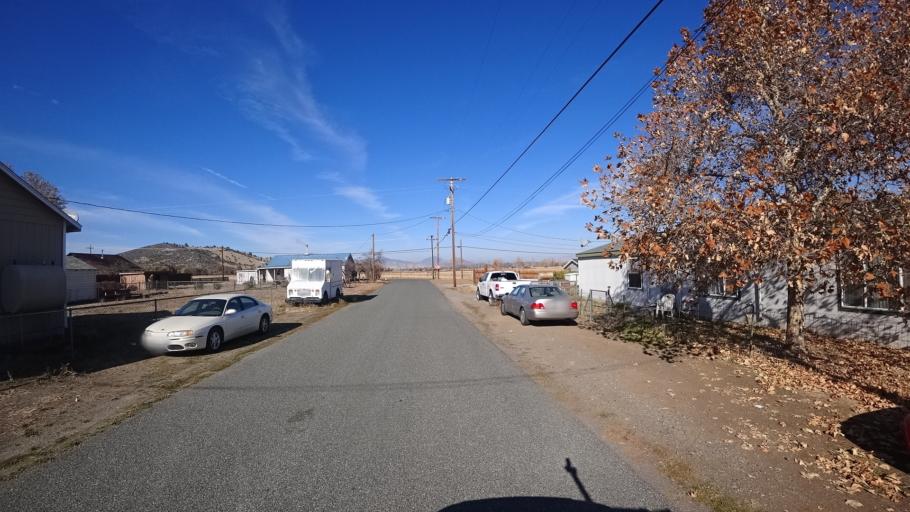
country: US
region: California
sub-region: Siskiyou County
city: Montague
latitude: 41.6465
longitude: -122.5250
